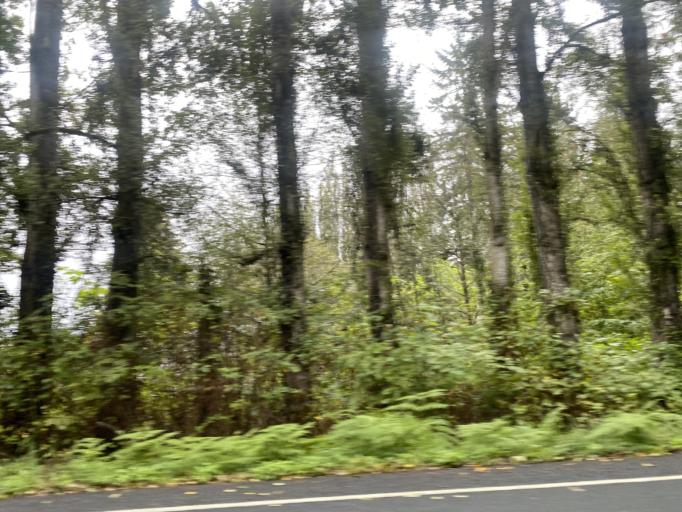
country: US
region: Washington
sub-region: Island County
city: Langley
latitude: 48.0436
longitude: -122.4316
